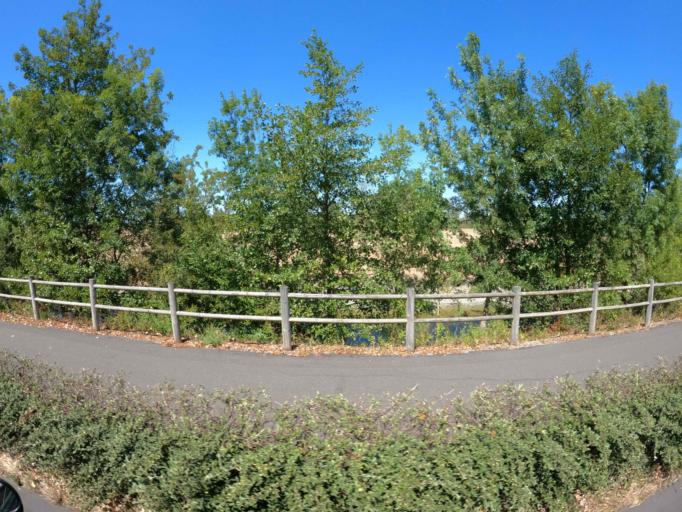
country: FR
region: Pays de la Loire
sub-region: Departement de la Vendee
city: Sallertaine
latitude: 46.8274
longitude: -1.9488
